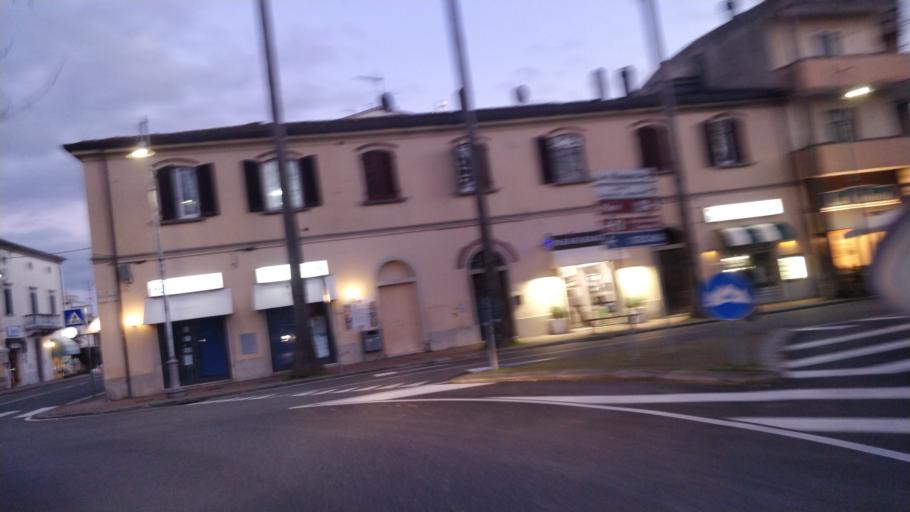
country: IT
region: Tuscany
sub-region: Provincia di Livorno
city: Vada
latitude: 43.3516
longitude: 10.4568
